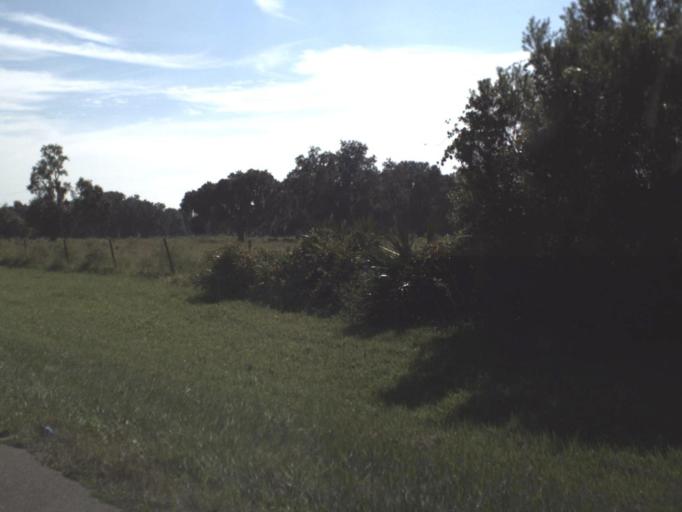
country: US
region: Florida
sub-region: Hardee County
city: Wauchula
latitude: 27.5514
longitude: -81.7641
